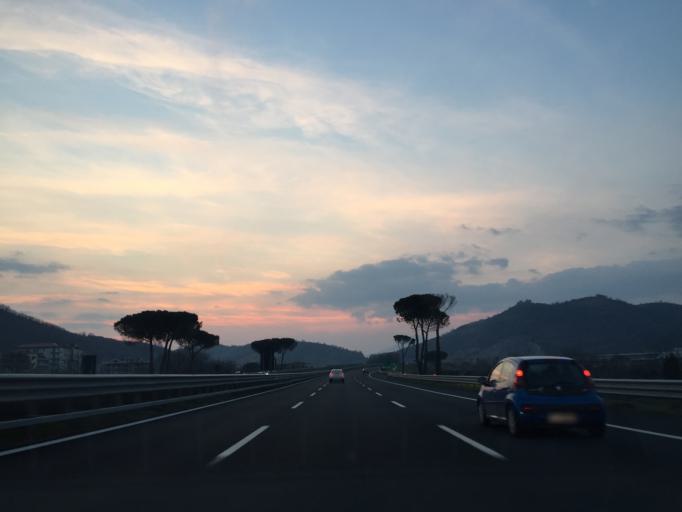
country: IT
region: Campania
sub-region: Provincia di Salerno
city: Casali-San Potito
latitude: 40.7673
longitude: 14.6805
